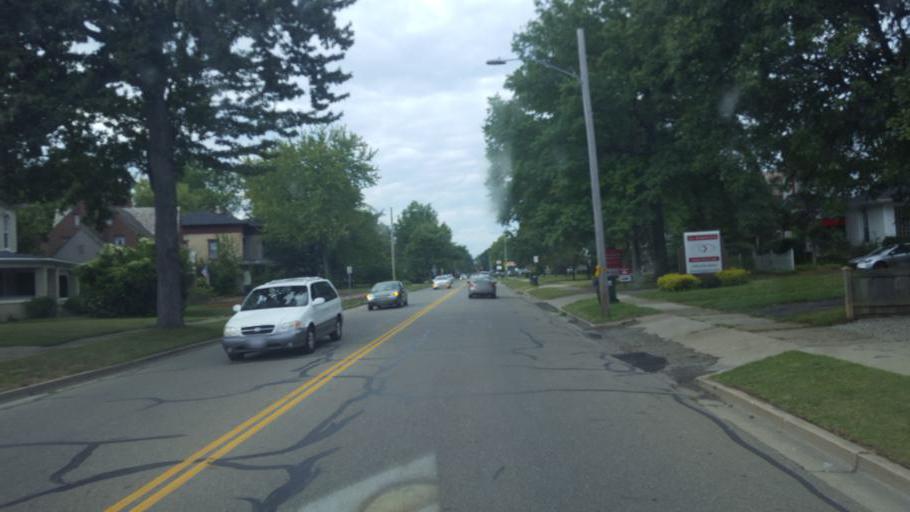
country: US
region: Ohio
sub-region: Tuscarawas County
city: Dover
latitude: 40.5246
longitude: -81.4789
